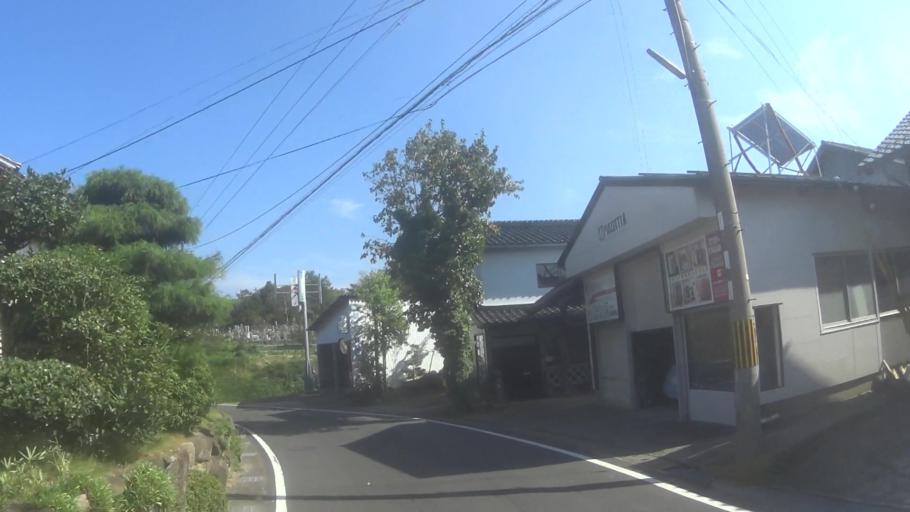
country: JP
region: Kyoto
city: Miyazu
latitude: 35.6801
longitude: 135.1025
